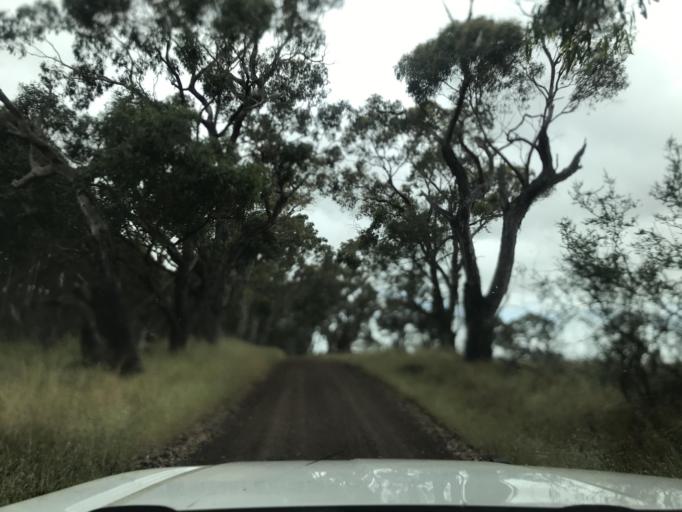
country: AU
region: South Australia
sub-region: Wattle Range
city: Penola
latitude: -37.2345
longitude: 141.4410
